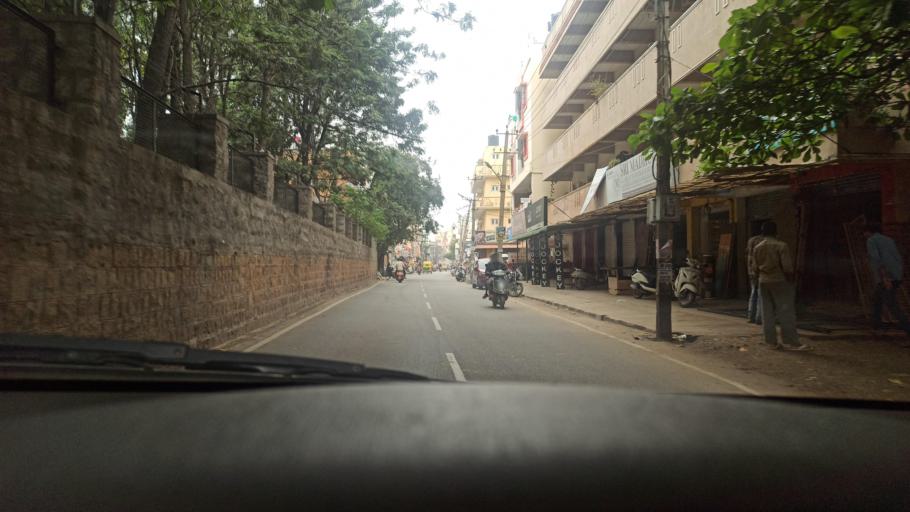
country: IN
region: Karnataka
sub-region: Bangalore Urban
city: Bangalore
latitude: 12.9896
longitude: 77.6797
